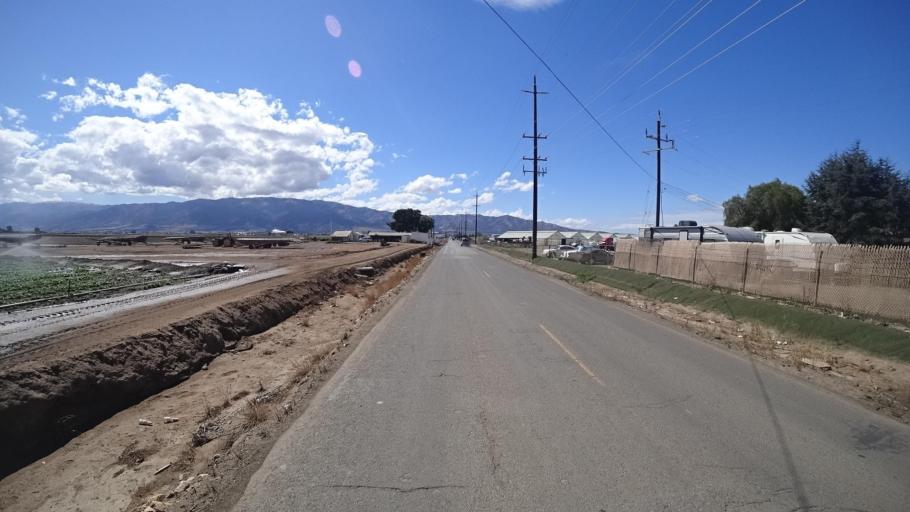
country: US
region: California
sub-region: Monterey County
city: Chualar
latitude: 36.6193
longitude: -121.5574
